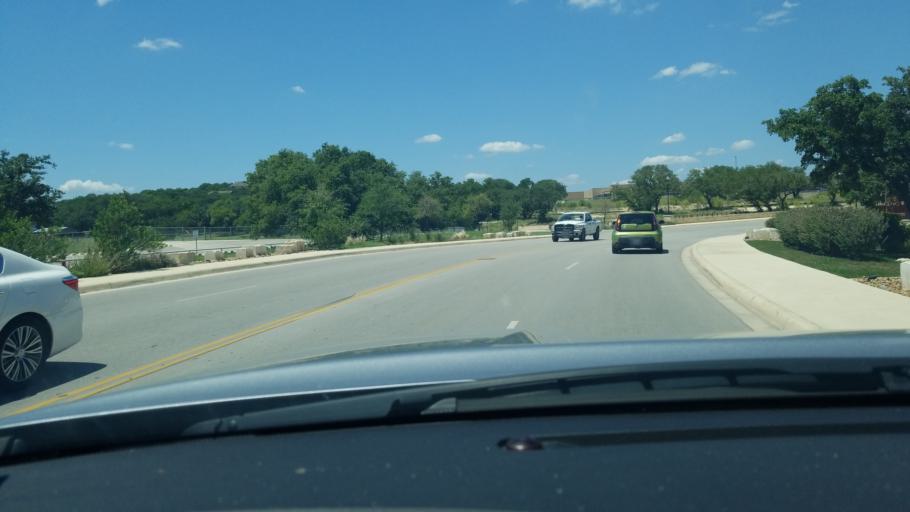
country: US
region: Texas
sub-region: Comal County
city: Bulverde
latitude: 29.7984
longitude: -98.4228
